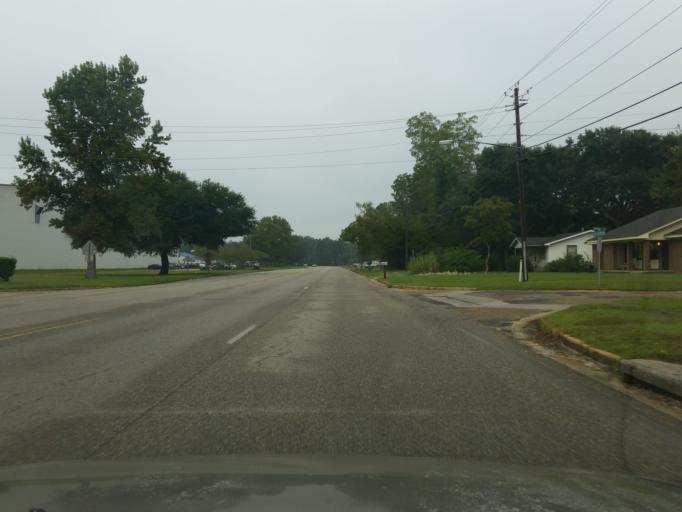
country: US
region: Alabama
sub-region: Baldwin County
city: Bay Minette
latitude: 30.8658
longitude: -87.7853
